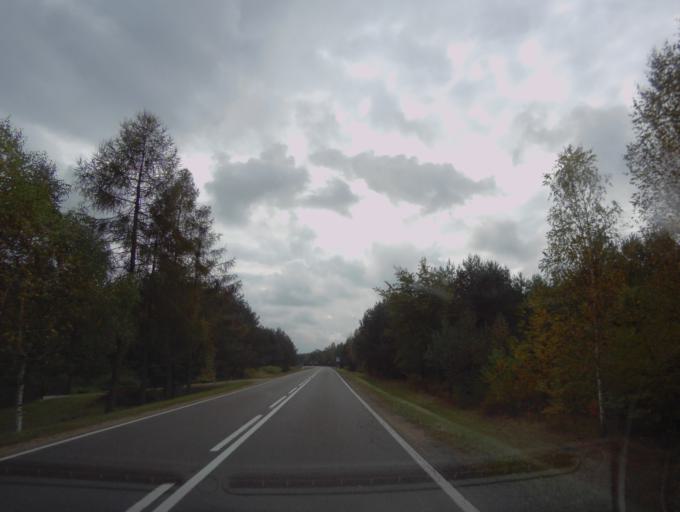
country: PL
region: Subcarpathian Voivodeship
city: Nowa Sarzyna
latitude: 50.3379
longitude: 22.3306
